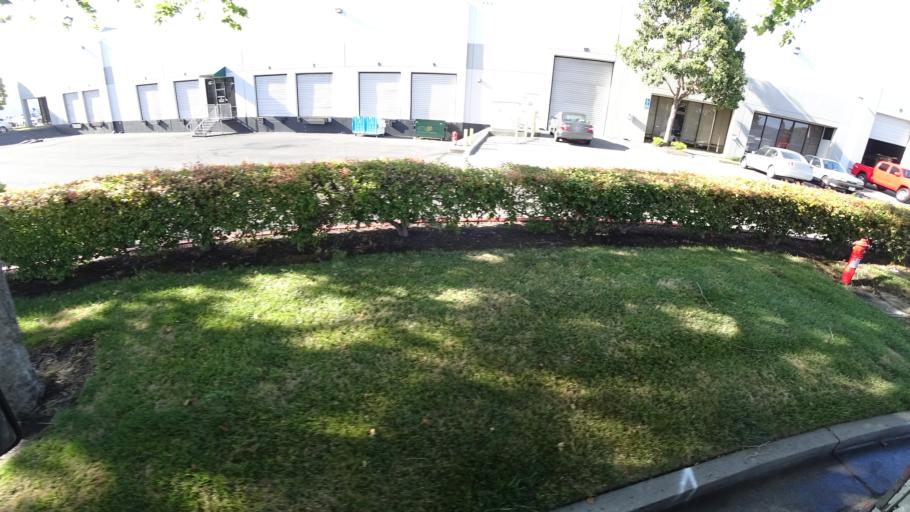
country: US
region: California
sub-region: Alameda County
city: San Lorenzo
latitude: 37.6432
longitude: -122.1223
